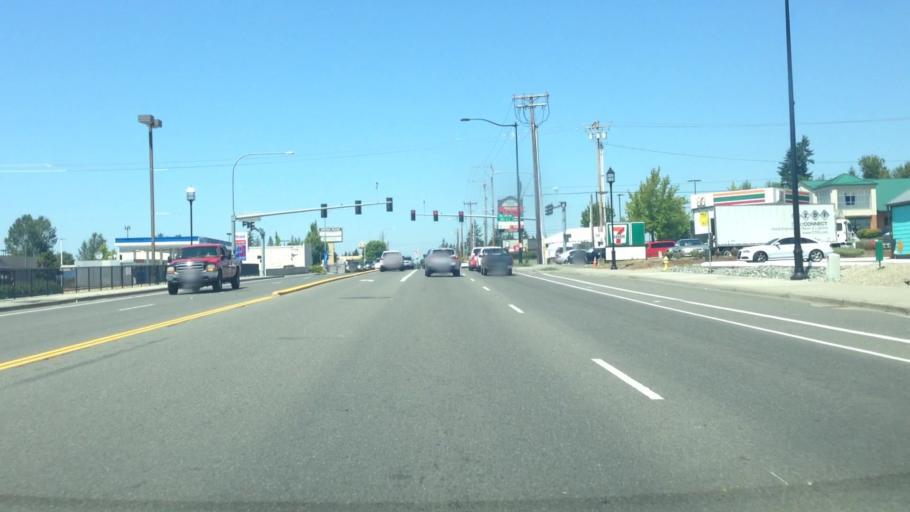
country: US
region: Washington
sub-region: Pierce County
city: Edgewood
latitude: 47.2491
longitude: -122.2938
